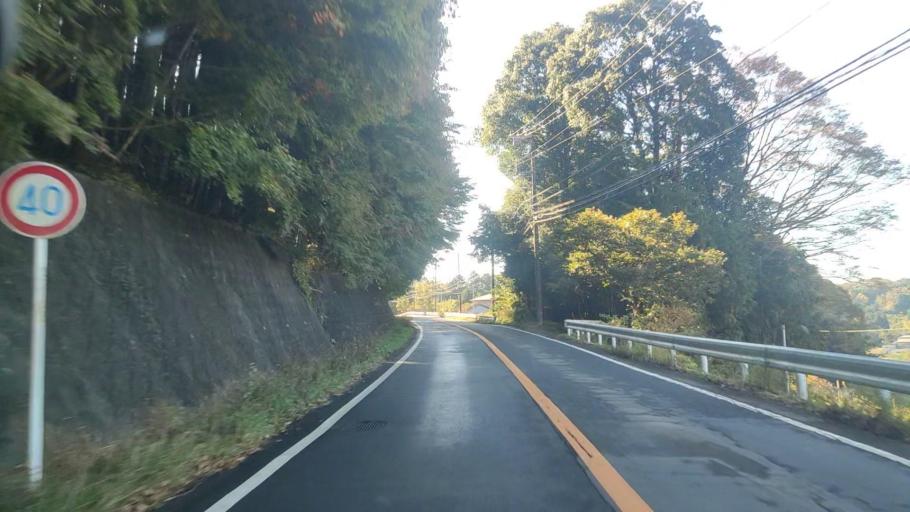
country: JP
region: Shizuoka
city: Atami
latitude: 35.0262
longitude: 139.0126
